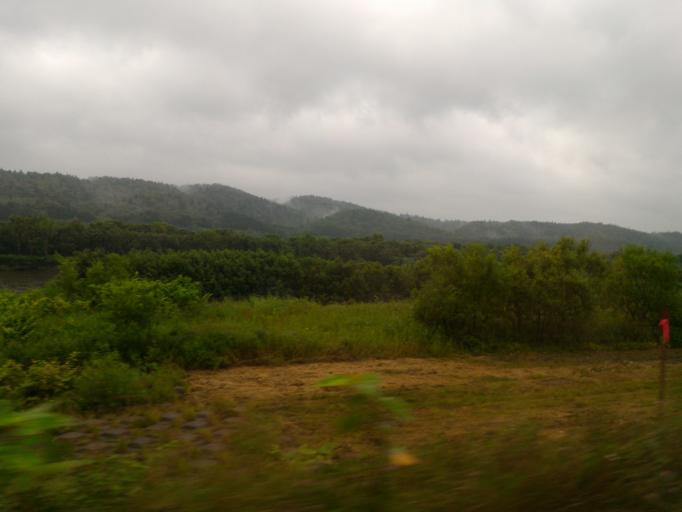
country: JP
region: Hokkaido
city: Nayoro
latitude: 44.7564
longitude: 142.0483
